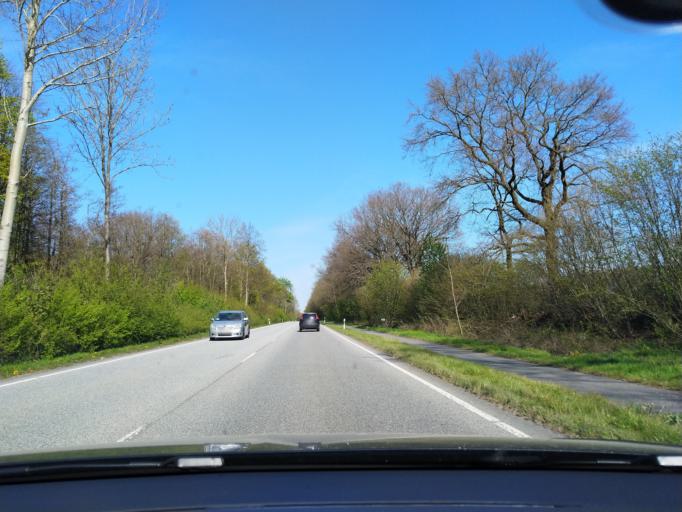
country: DE
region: Schleswig-Holstein
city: Stapelfeld
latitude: 53.6131
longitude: 10.2070
